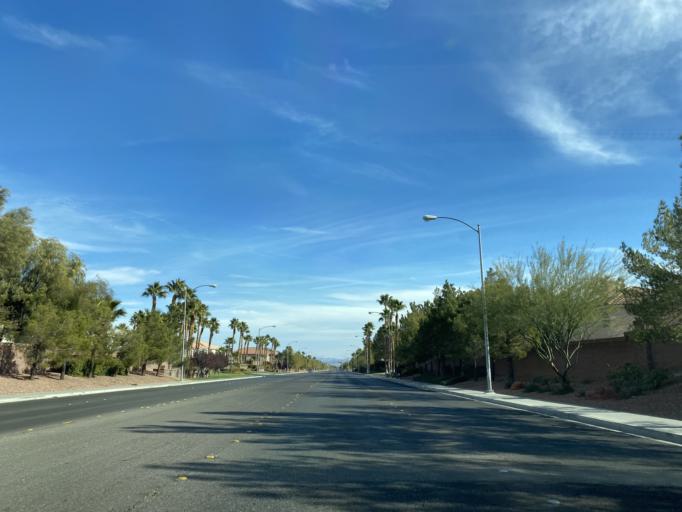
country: US
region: Nevada
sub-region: Clark County
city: Enterprise
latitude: 36.0487
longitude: -115.2393
